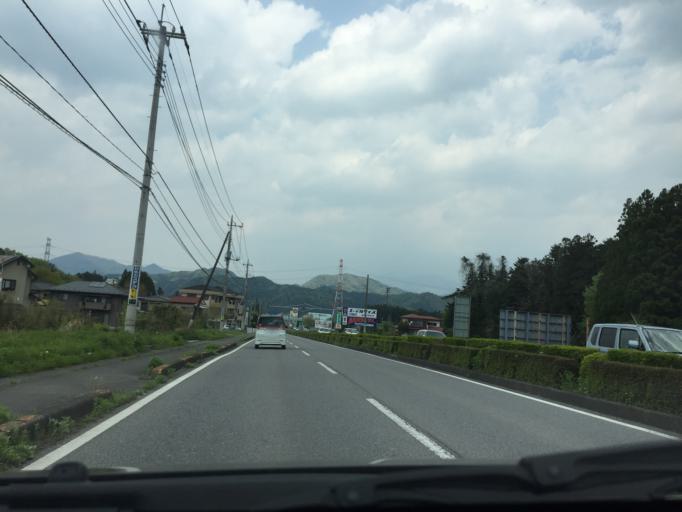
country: JP
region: Tochigi
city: Imaichi
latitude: 36.7588
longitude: 139.7163
